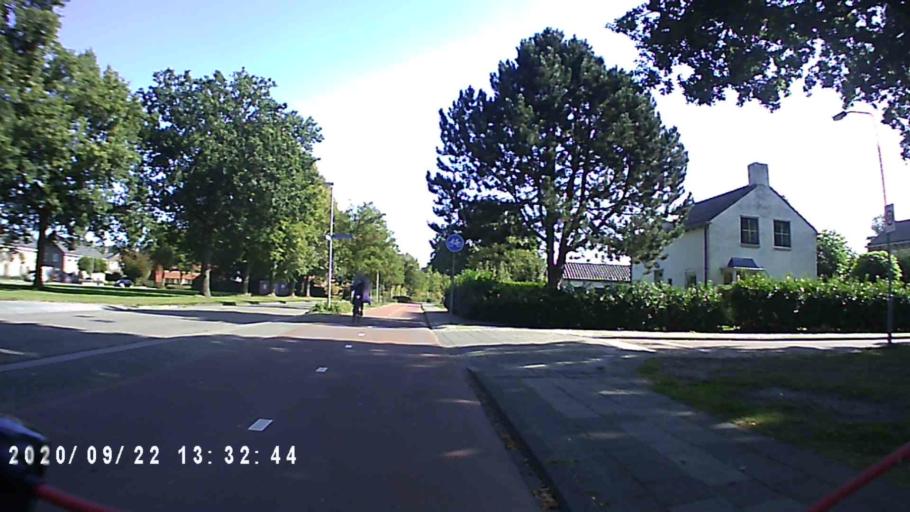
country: NL
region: Groningen
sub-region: Gemeente Leek
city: Leek
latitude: 53.1637
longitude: 6.3854
